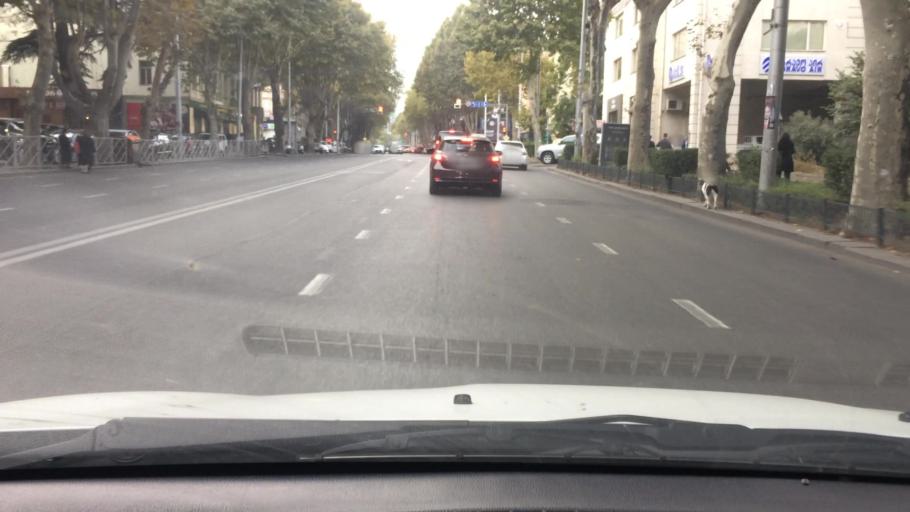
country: GE
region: T'bilisi
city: Tbilisi
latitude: 41.7096
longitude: 44.7691
